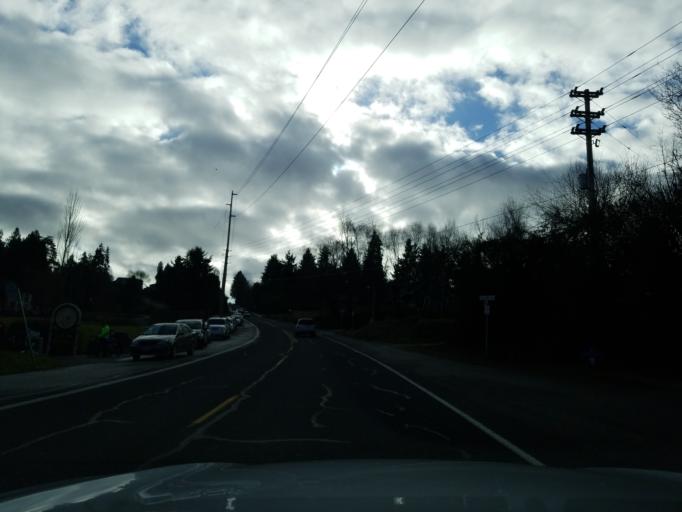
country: US
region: Washington
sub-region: Clark County
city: Felida
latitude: 45.7217
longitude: -122.7078
